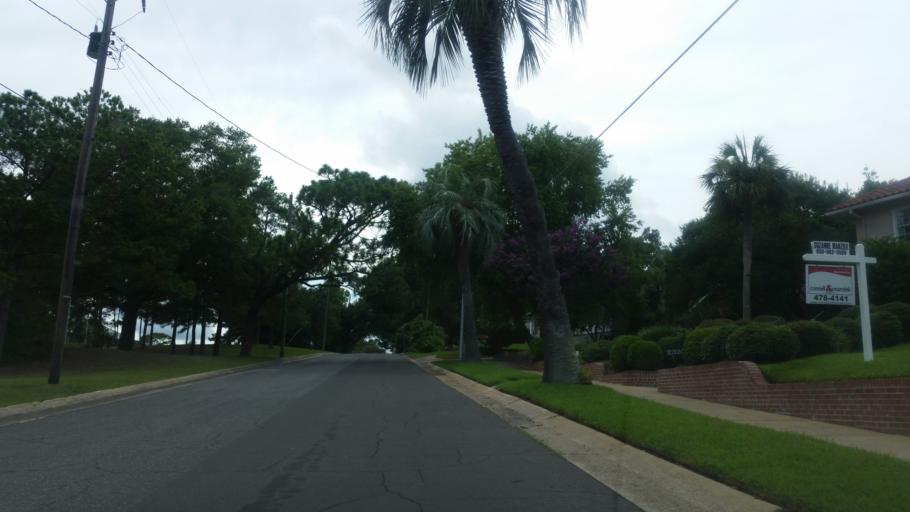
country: US
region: Florida
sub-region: Escambia County
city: East Pensacola Heights
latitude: 30.4338
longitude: -87.1882
